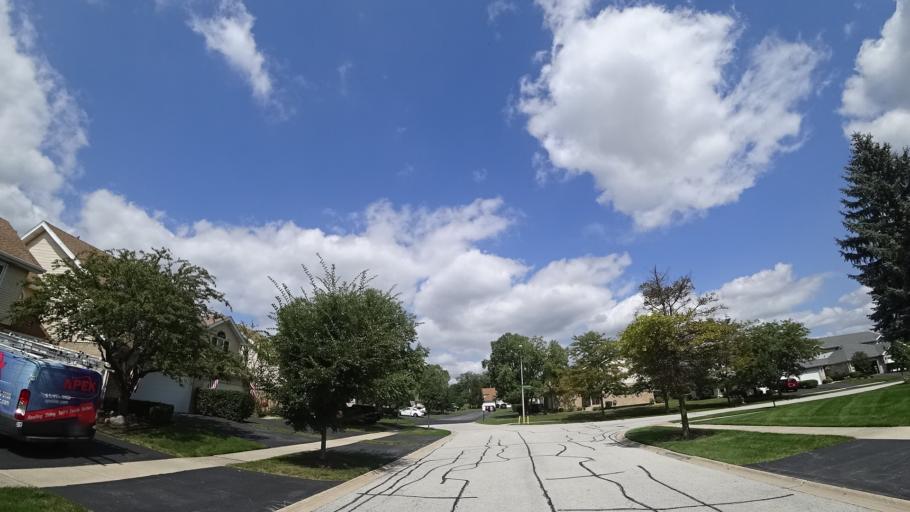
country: US
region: Illinois
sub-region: Cook County
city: Orland Hills
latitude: 41.5706
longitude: -87.8488
